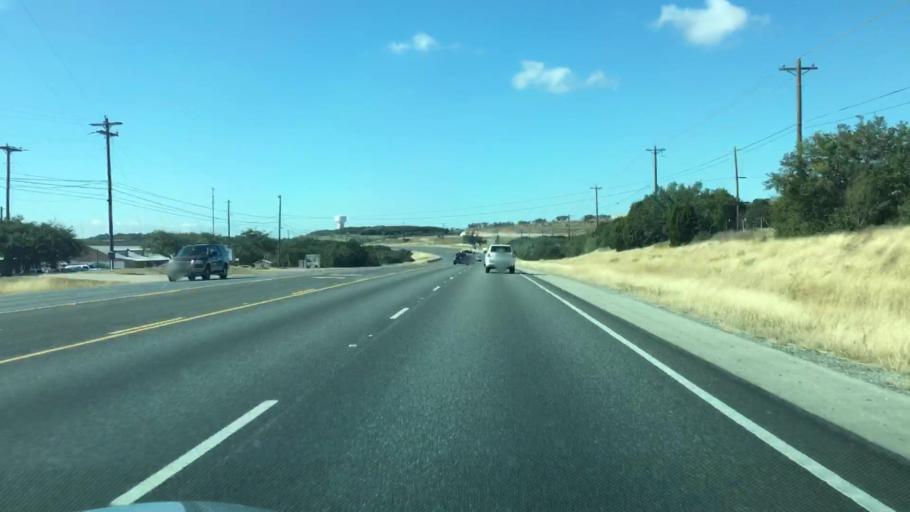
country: US
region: Texas
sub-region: Hays County
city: Dripping Springs
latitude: 30.1949
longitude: -98.0545
